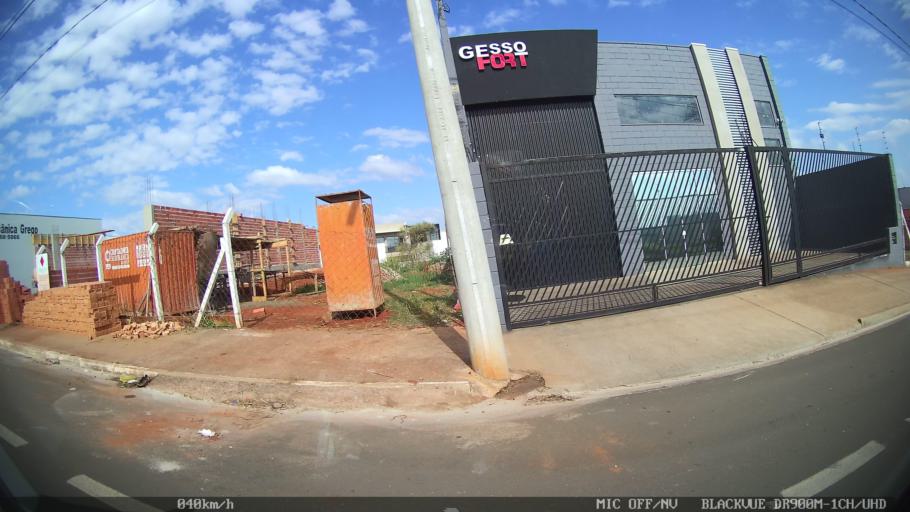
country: BR
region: Sao Paulo
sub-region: Americana
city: Americana
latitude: -22.7224
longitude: -47.3246
